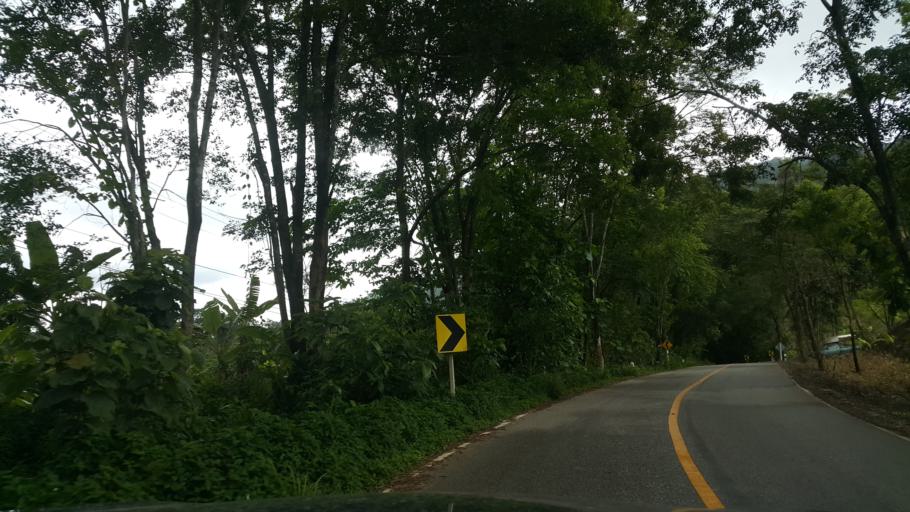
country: TH
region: Loei
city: Na Haeo
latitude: 17.4884
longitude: 100.8061
